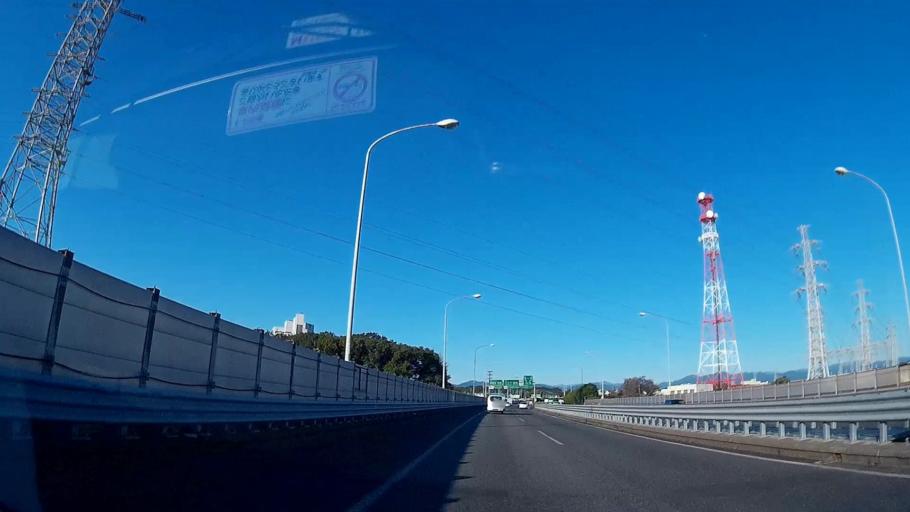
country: JP
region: Tokyo
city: Hino
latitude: 35.6746
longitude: 139.3608
